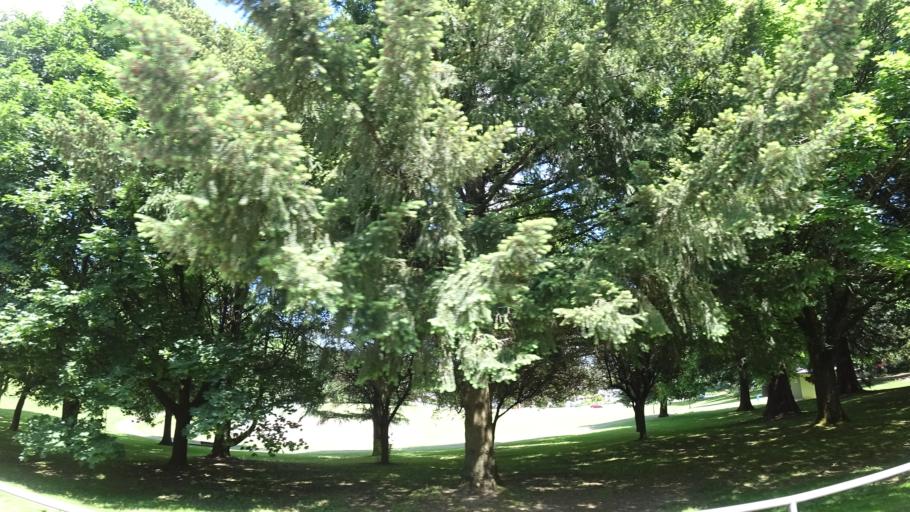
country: US
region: Oregon
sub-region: Washington County
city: Garden Home-Whitford
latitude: 45.4702
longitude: -122.7014
